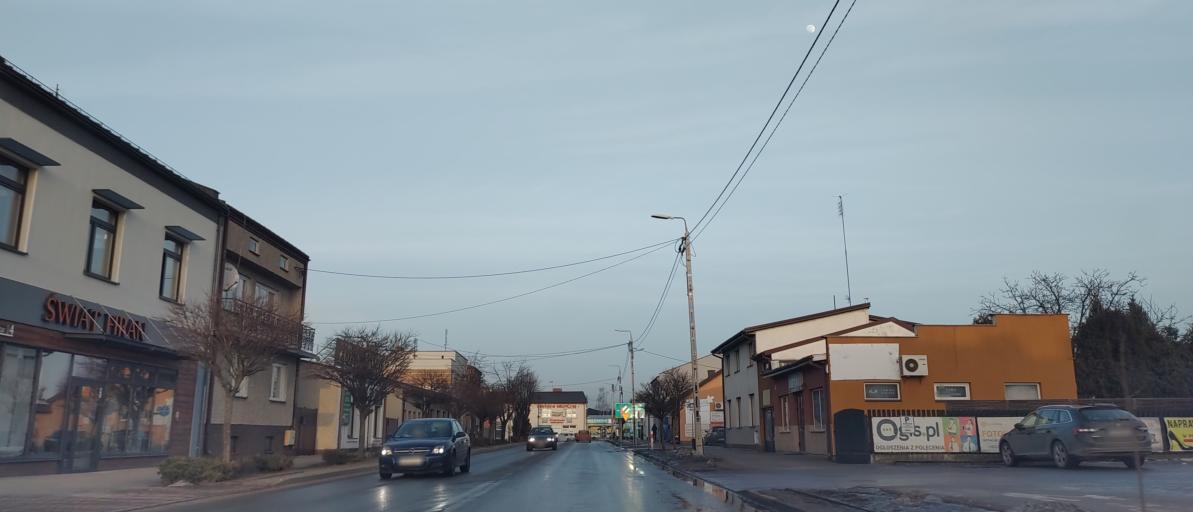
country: PL
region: Masovian Voivodeship
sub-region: Powiat bialobrzeski
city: Bialobrzegi
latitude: 51.6456
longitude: 20.9547
